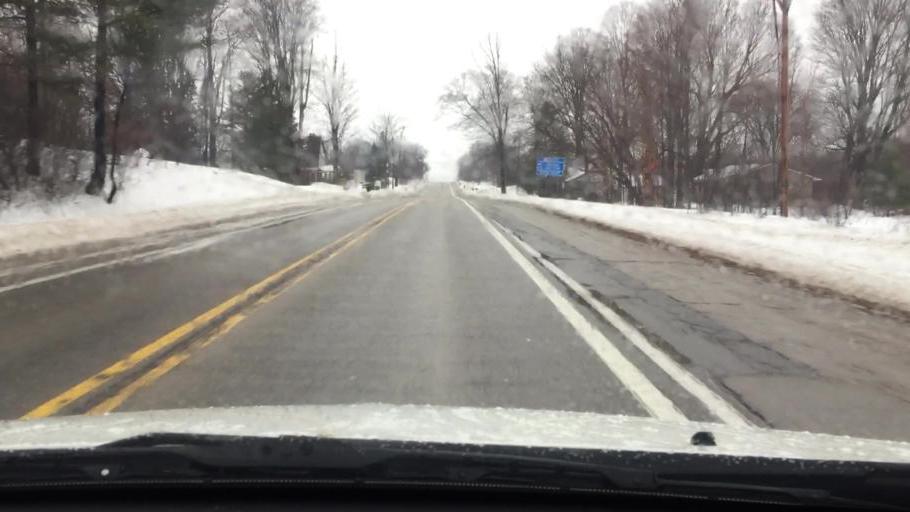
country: US
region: Michigan
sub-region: Charlevoix County
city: East Jordan
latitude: 45.1431
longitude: -85.1398
